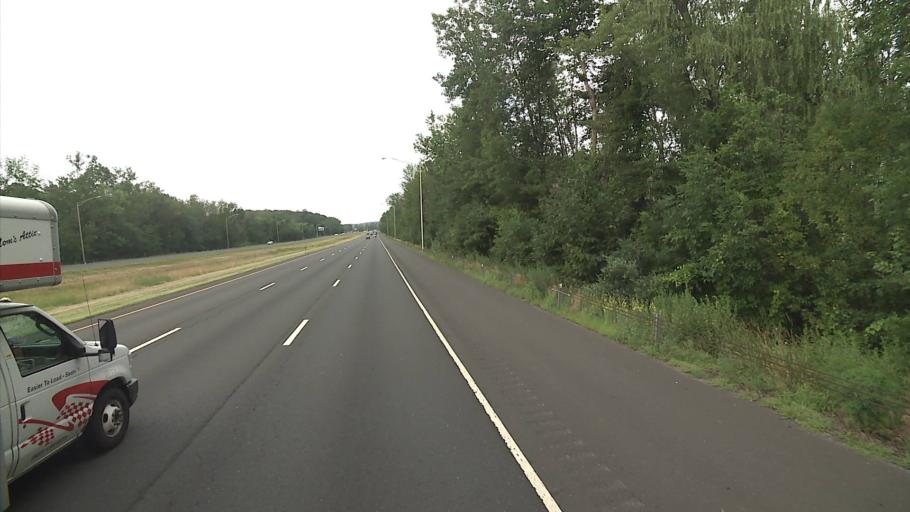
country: US
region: Connecticut
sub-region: Hartford County
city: Farmington
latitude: 41.6982
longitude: -72.8081
